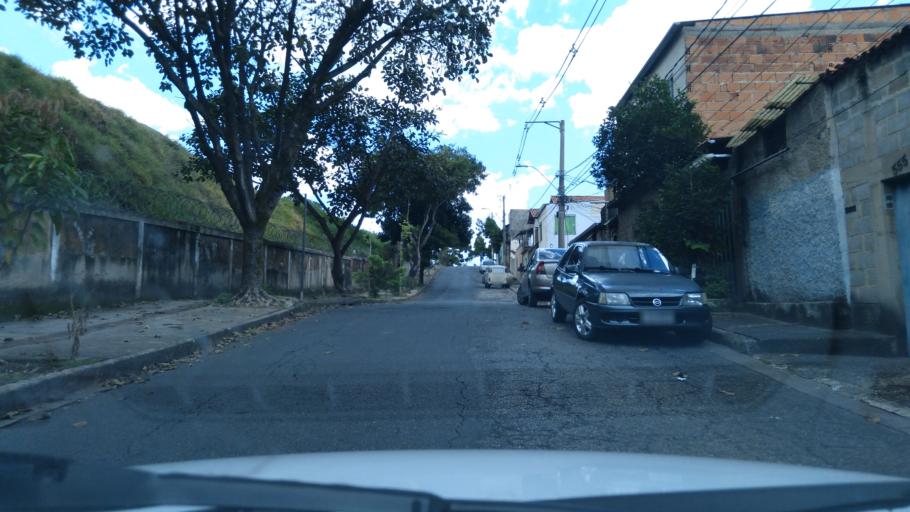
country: BR
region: Minas Gerais
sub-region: Belo Horizonte
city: Belo Horizonte
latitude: -19.9162
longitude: -43.8962
